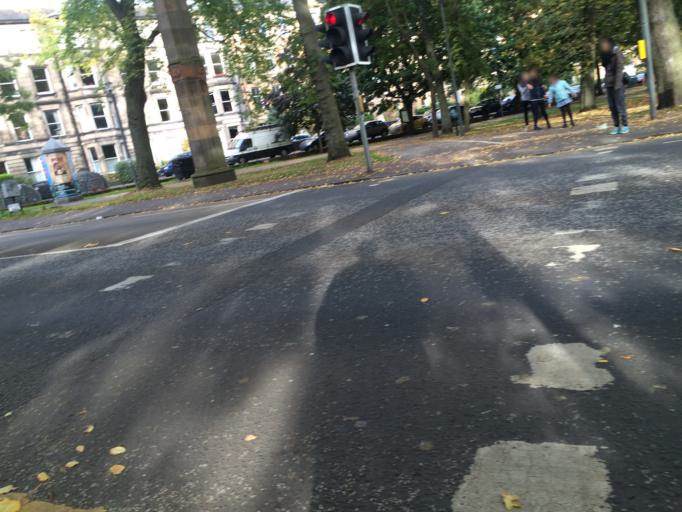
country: GB
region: Scotland
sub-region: Edinburgh
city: Edinburgh
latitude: 55.9419
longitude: -3.2004
